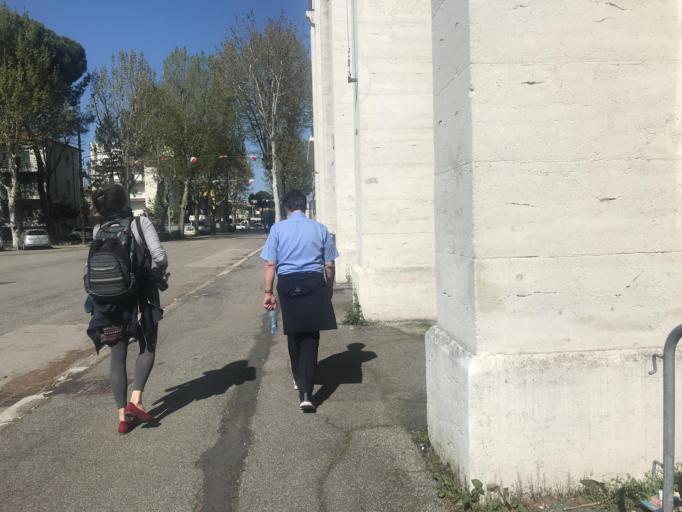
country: IT
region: Emilia-Romagna
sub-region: Provincia di Rimini
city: Rimini
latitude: 44.0533
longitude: 12.5762
